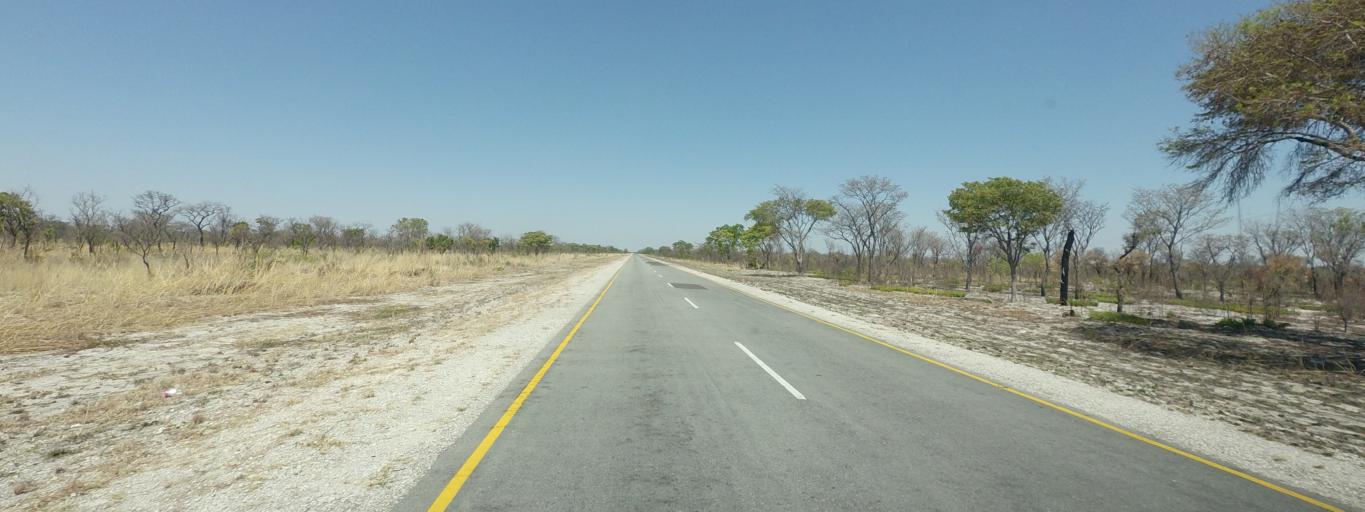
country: BW
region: North West
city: Shakawe
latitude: -17.9684
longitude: 22.5133
